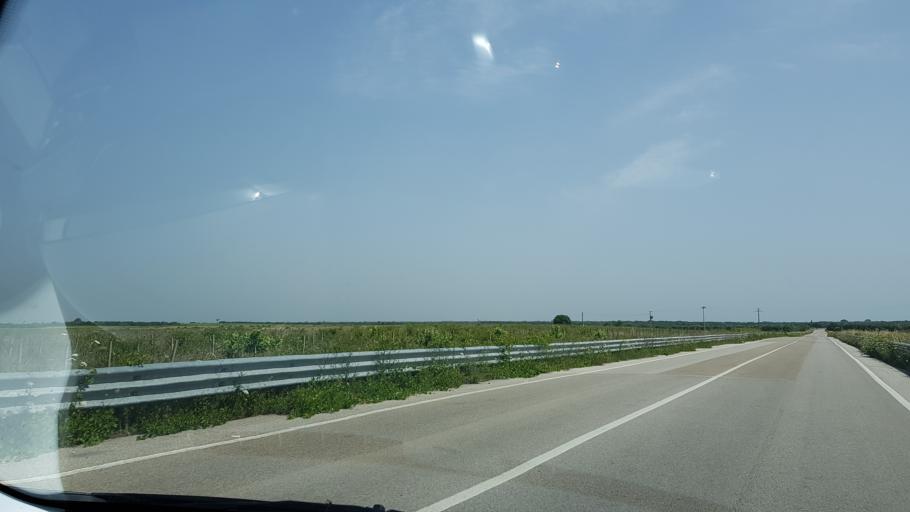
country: IT
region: Apulia
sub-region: Provincia di Brindisi
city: San Pancrazio Salentino
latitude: 40.4820
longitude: 17.8354
